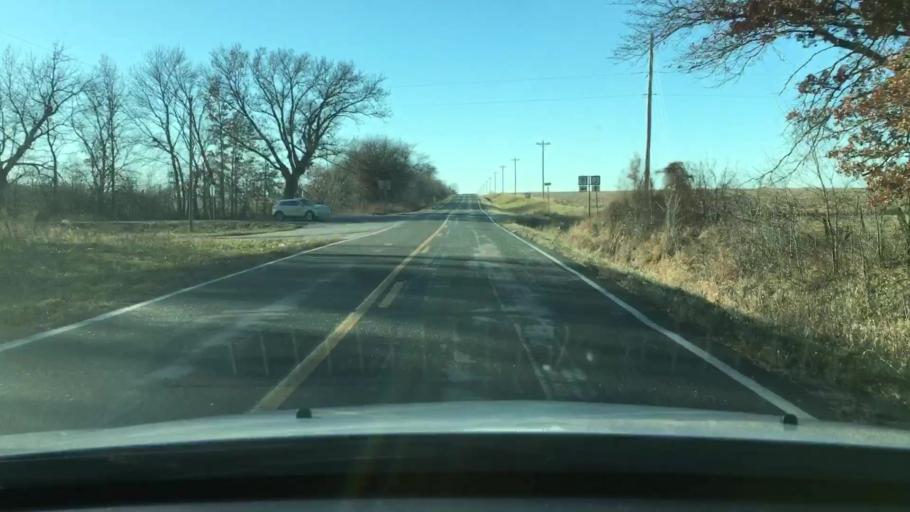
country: US
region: Missouri
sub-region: Audrain County
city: Mexico
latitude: 39.2814
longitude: -91.7196
